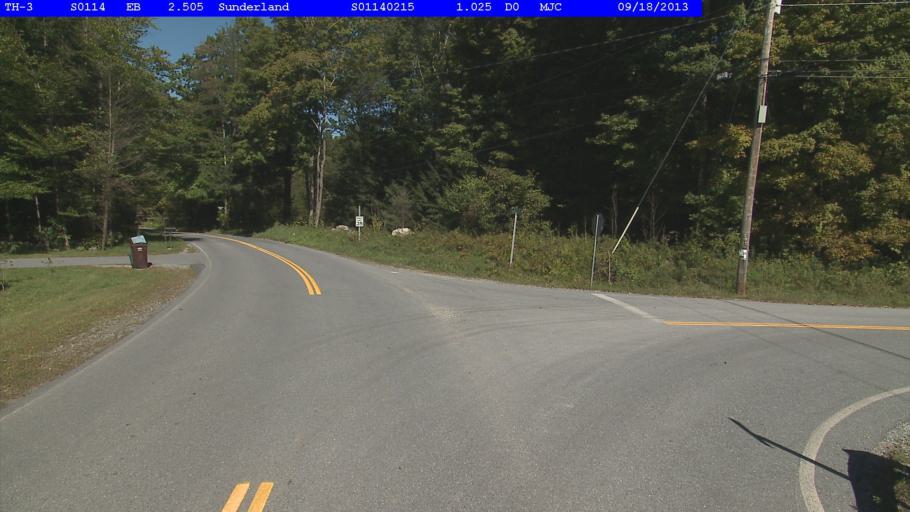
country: US
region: Vermont
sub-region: Bennington County
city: Arlington
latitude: 43.0576
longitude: -73.1188
